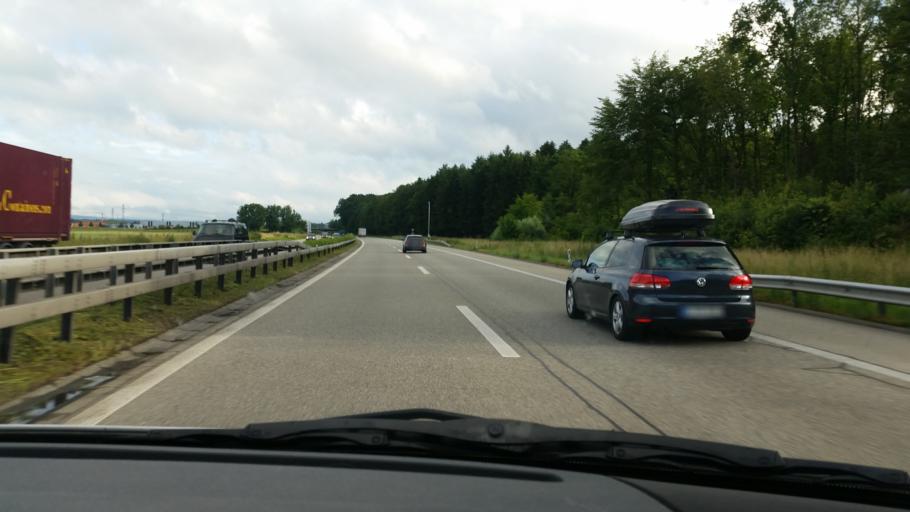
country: CH
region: Solothurn
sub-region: Bezirk Wasseramt
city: Luterbach
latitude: 47.2105
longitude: 7.6005
